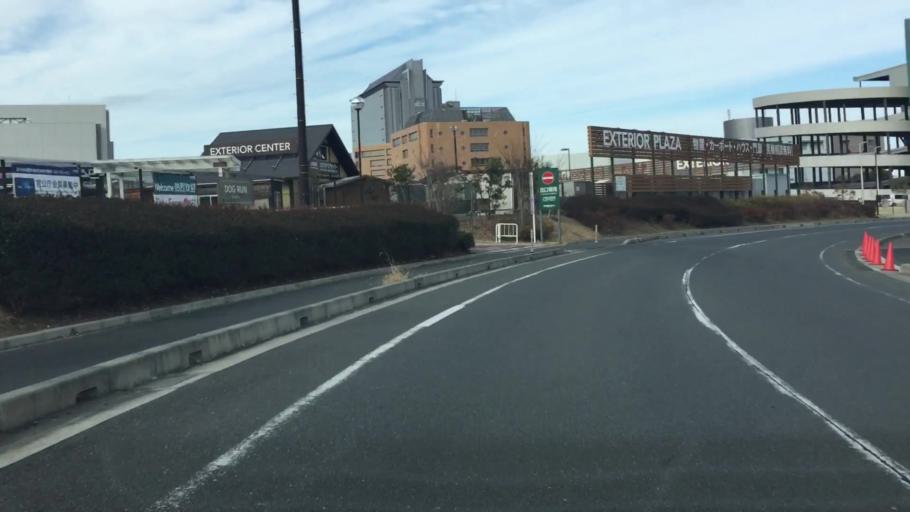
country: JP
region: Chiba
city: Shiroi
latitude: 35.8049
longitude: 140.1239
